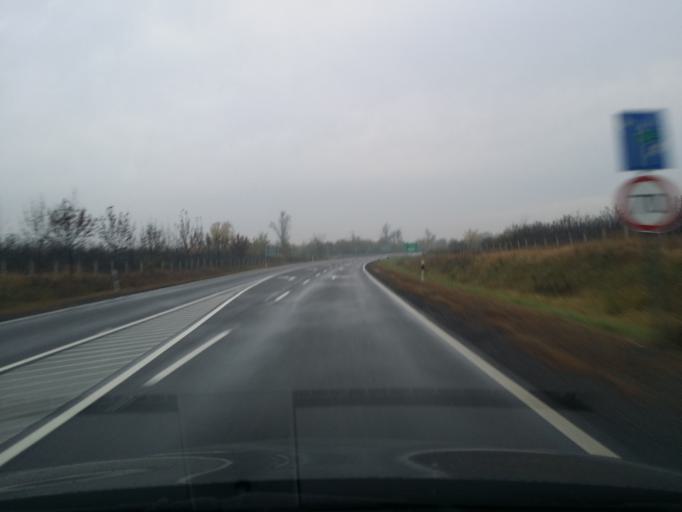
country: HU
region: Szabolcs-Szatmar-Bereg
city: Nyirpazony
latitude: 48.0184
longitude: 21.8429
